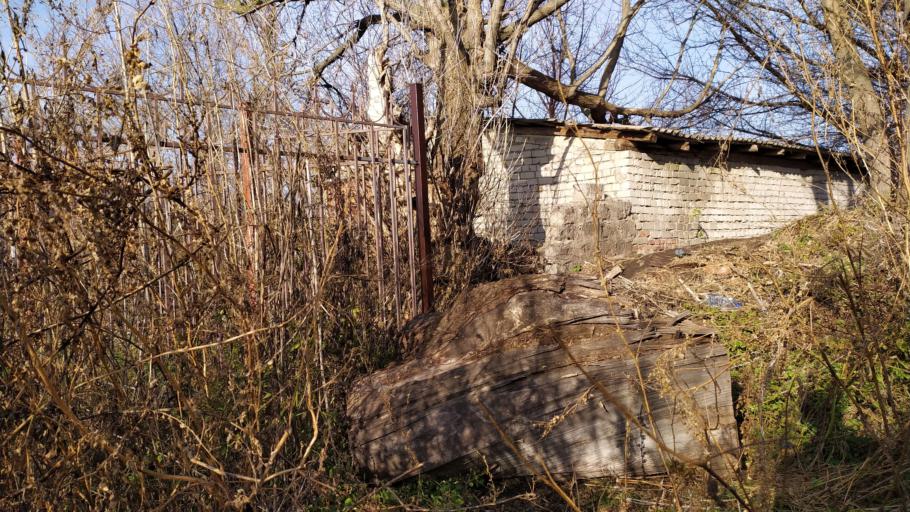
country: RU
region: Kursk
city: Kursk
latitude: 51.6437
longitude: 36.1315
